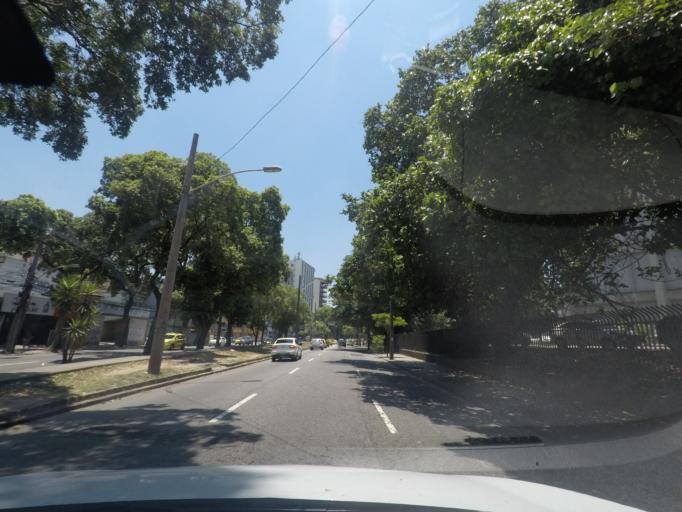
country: BR
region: Rio de Janeiro
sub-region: Rio De Janeiro
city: Rio de Janeiro
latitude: -22.9115
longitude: -43.2374
